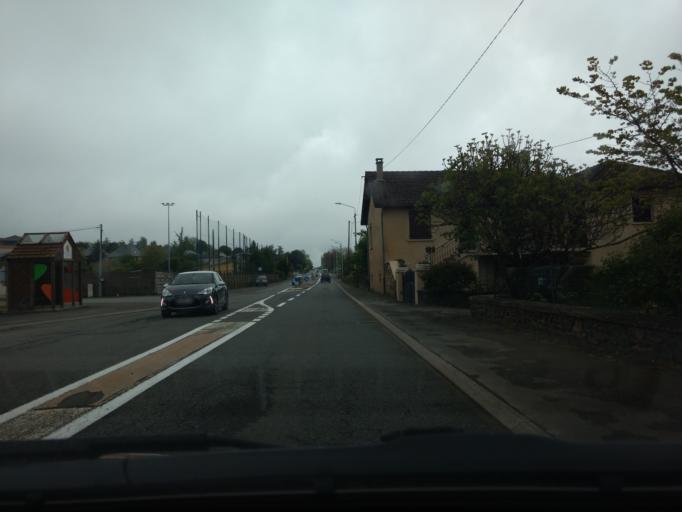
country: FR
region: Midi-Pyrenees
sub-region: Departement de l'Aveyron
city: Montbazens
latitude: 44.4676
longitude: 2.2247
